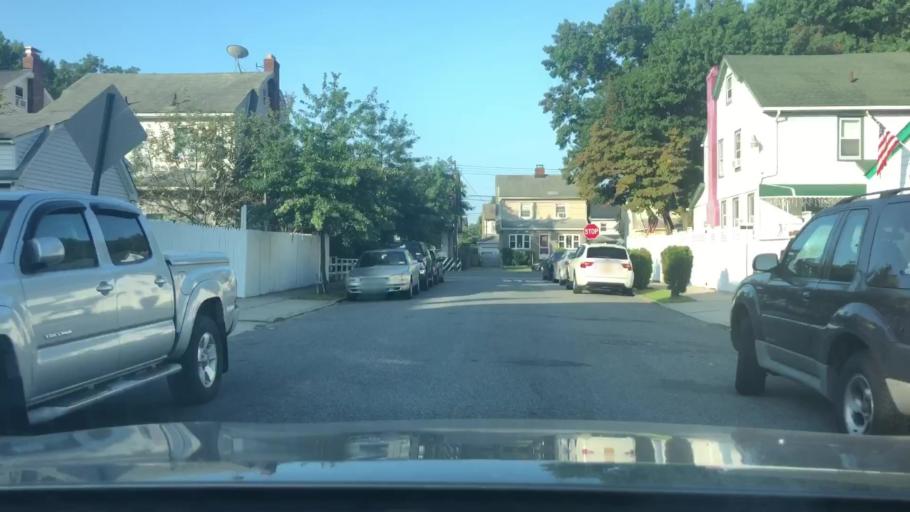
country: US
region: New York
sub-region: Nassau County
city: Bellerose Terrace
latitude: 40.7240
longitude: -73.7377
